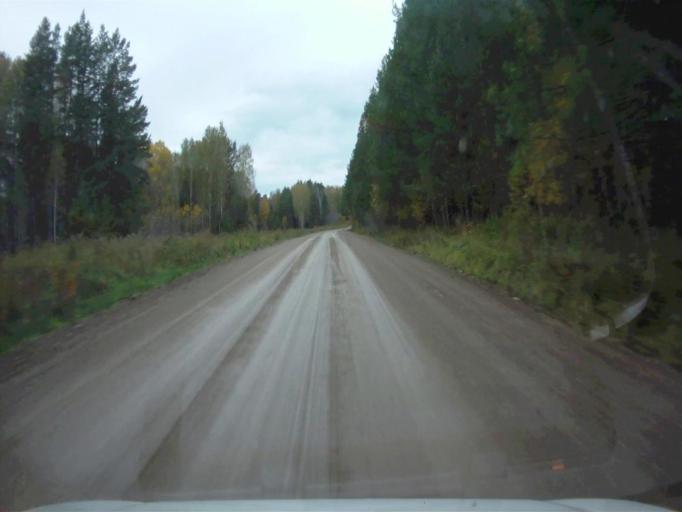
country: RU
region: Chelyabinsk
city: Nyazepetrovsk
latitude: 56.0958
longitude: 59.4005
